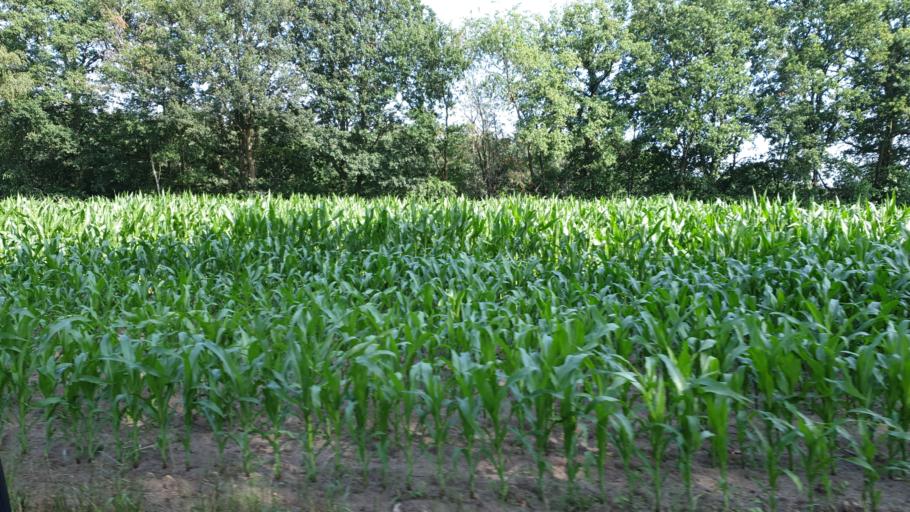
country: BE
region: Flanders
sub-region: Provincie Antwerpen
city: Geel
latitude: 51.1839
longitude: 5.0126
